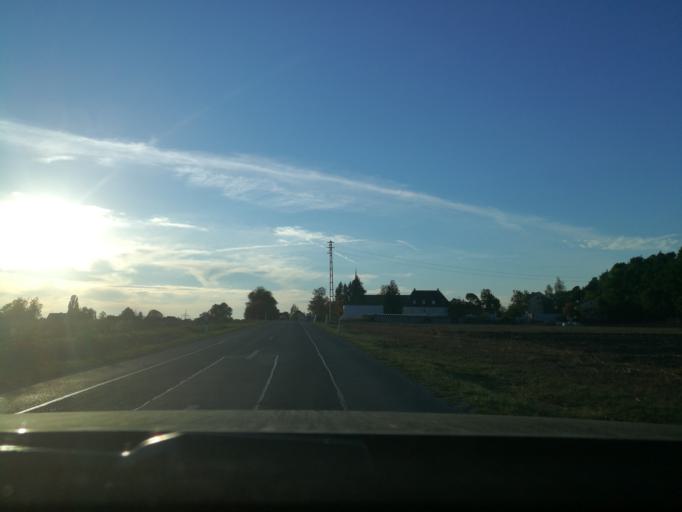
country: DE
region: Bavaria
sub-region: Regierungsbezirk Mittelfranken
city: Furth
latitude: 49.5243
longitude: 10.9814
